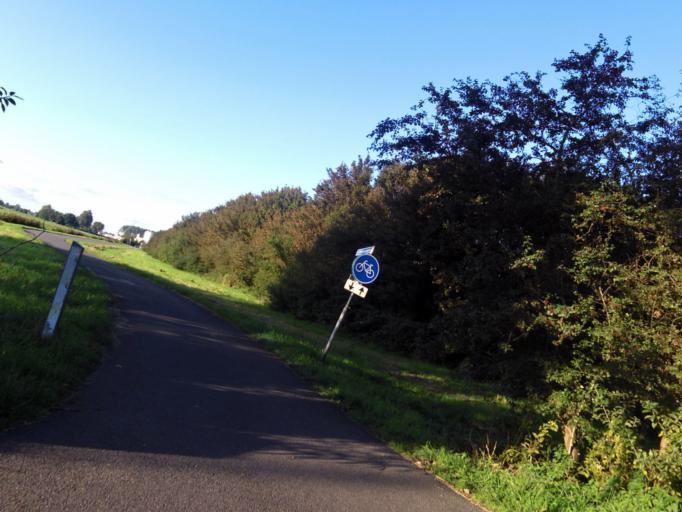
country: NL
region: South Holland
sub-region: Gemeente Alphen aan den Rijn
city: Alphen aan den Rijn
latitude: 52.1440
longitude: 4.6447
